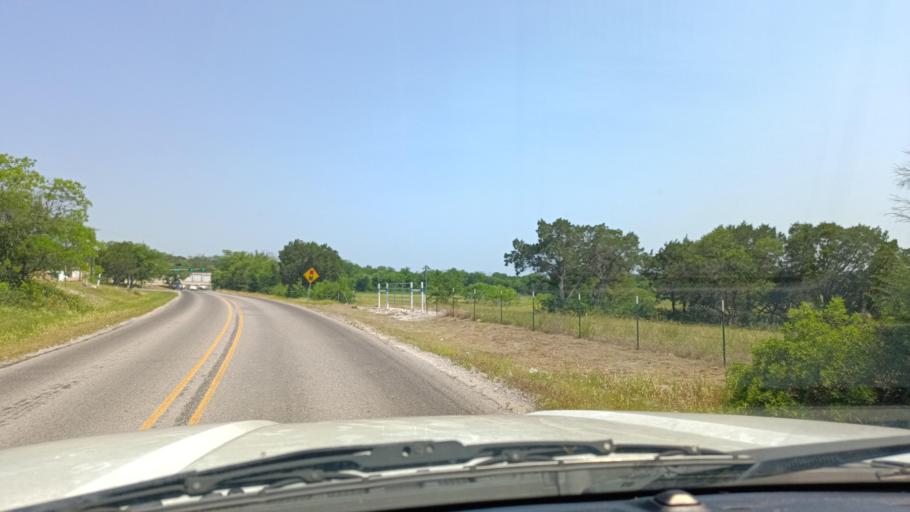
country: US
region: Texas
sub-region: Bell County
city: Belton
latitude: 31.1015
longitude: -97.5181
